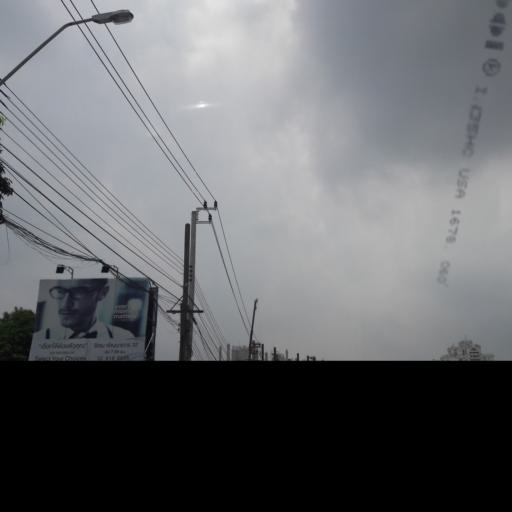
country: TH
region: Bangkok
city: Suan Luang
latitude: 13.7295
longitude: 100.6224
